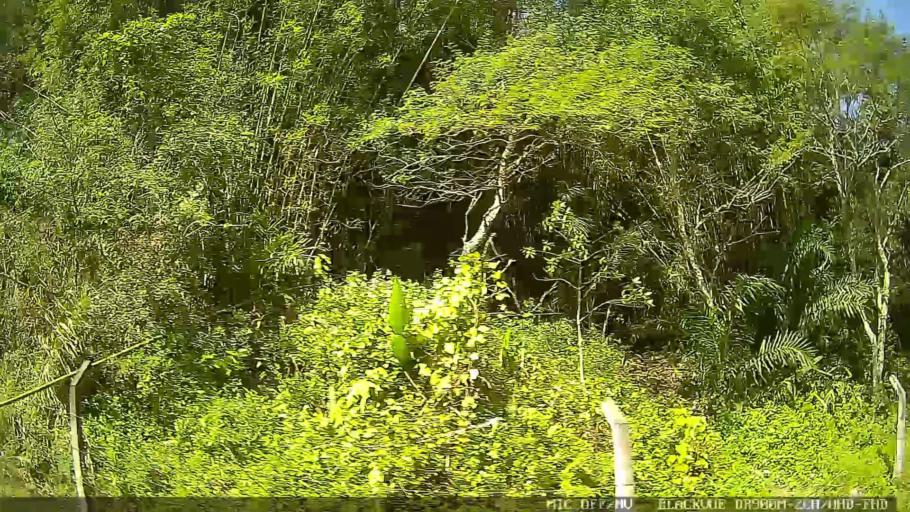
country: BR
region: Sao Paulo
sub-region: Guaruja
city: Guaruja
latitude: -24.0118
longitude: -46.3001
